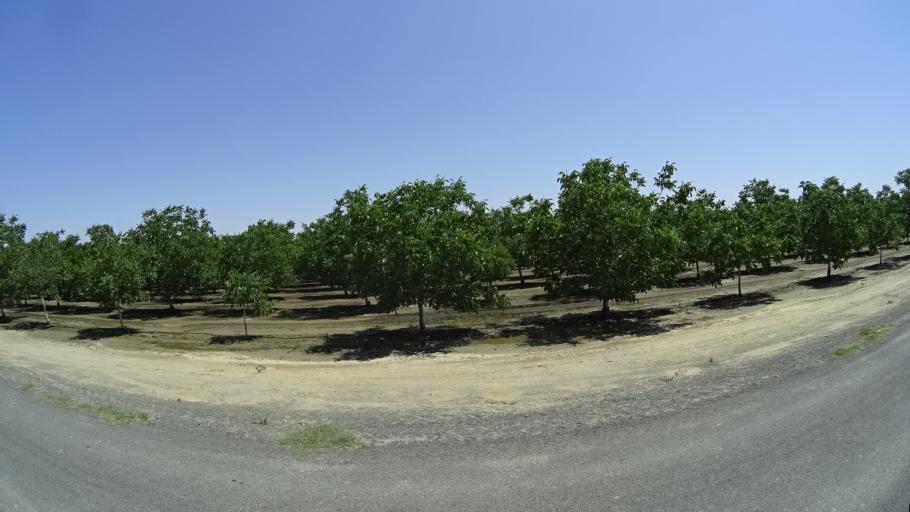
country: US
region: California
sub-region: Kings County
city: Armona
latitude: 36.2929
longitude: -119.7272
